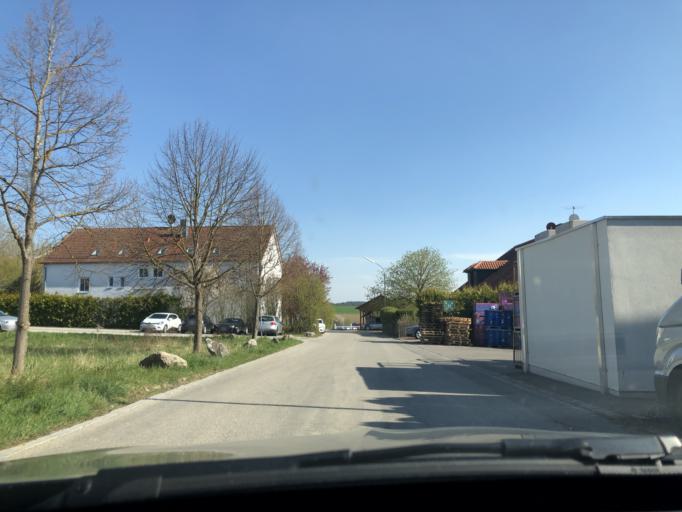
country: DE
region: Bavaria
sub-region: Upper Bavaria
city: Schweitenkirchen
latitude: 48.5003
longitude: 11.6061
